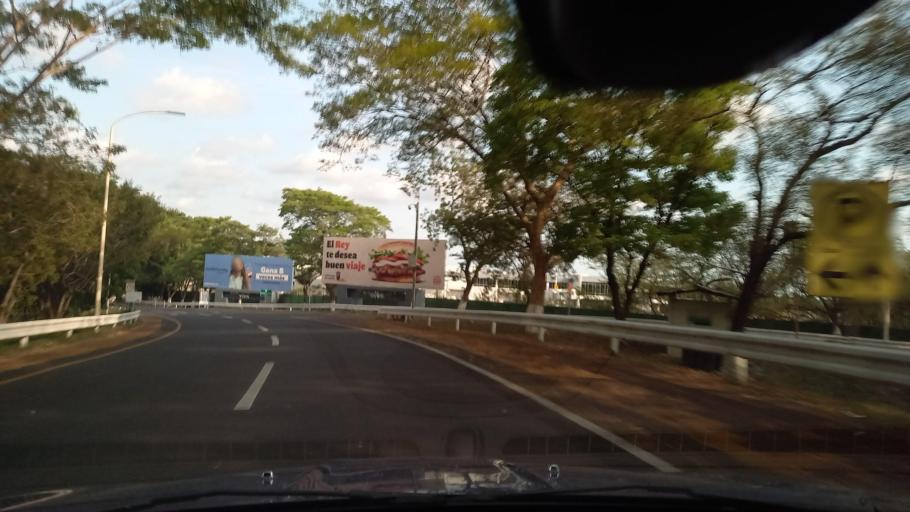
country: SV
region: La Paz
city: El Rosario
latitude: 13.4463
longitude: -89.0604
